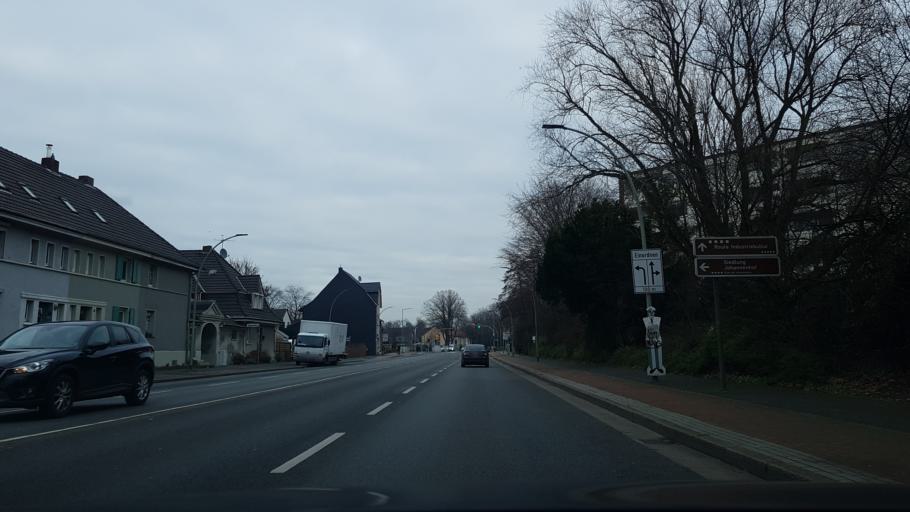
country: DE
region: North Rhine-Westphalia
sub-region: Regierungsbezirk Dusseldorf
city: Moers
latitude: 51.4513
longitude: 6.6971
